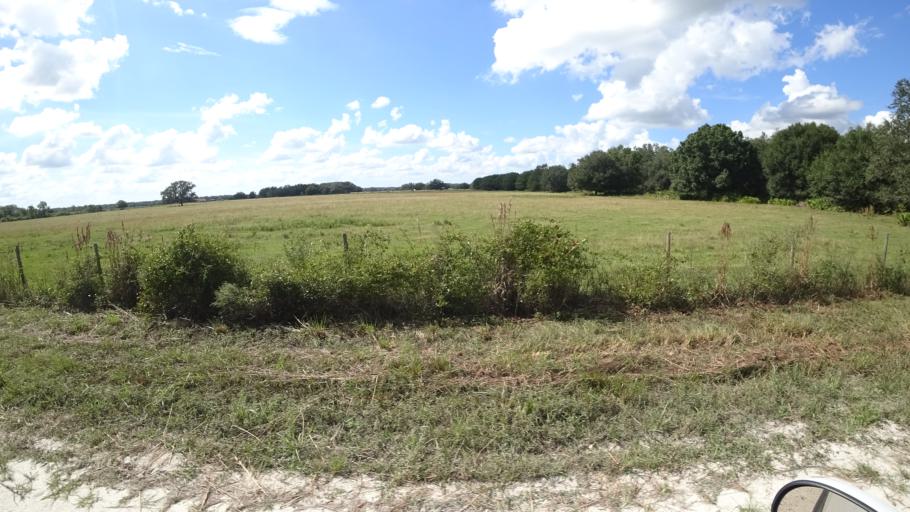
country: US
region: Florida
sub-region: DeSoto County
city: Arcadia
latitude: 27.3316
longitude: -82.1050
